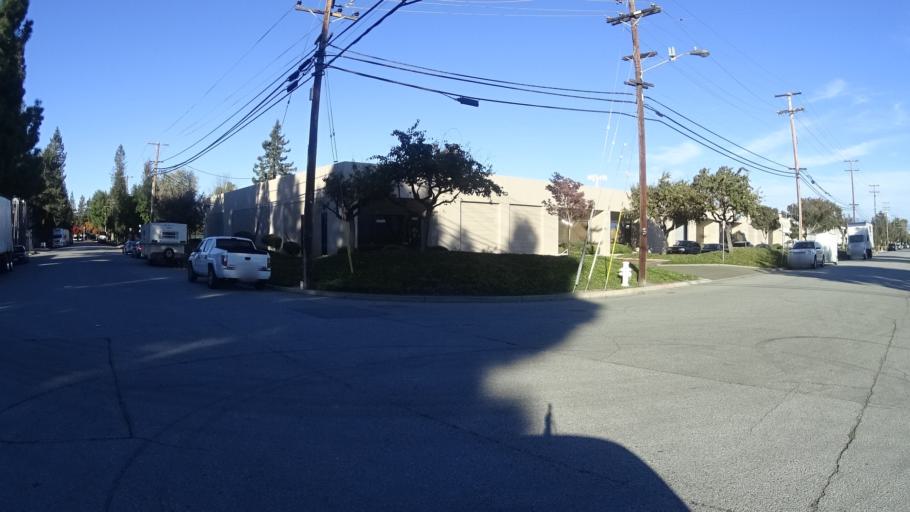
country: US
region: California
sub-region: Santa Clara County
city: Santa Clara
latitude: 37.3717
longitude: -121.9825
